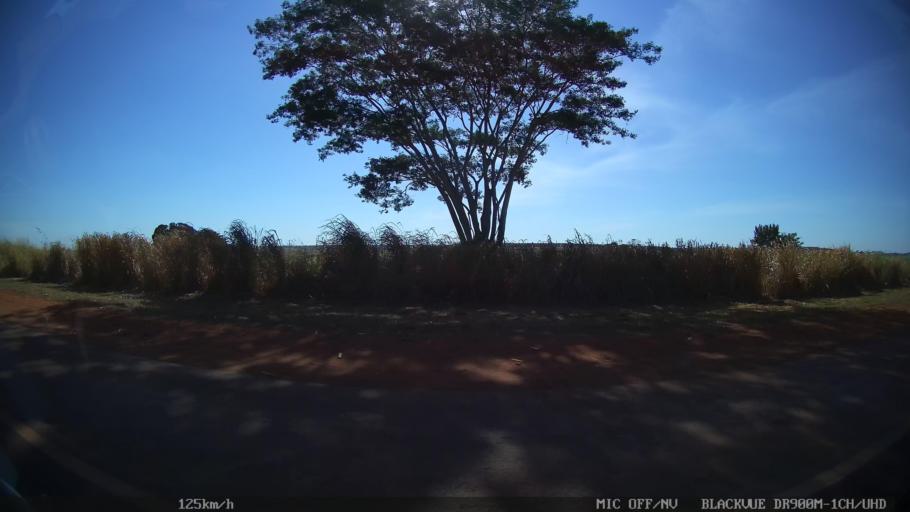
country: BR
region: Sao Paulo
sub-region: Olimpia
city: Olimpia
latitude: -20.6810
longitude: -48.8966
